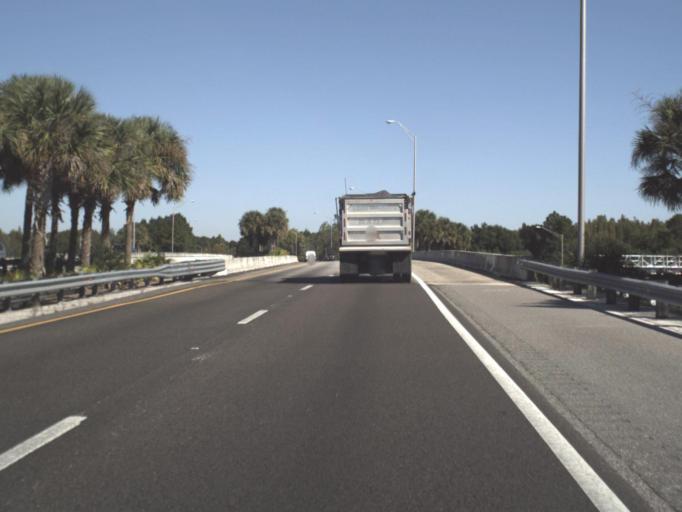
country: US
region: Florida
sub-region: Hillsborough County
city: Greater Northdale
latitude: 28.0969
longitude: -82.5430
